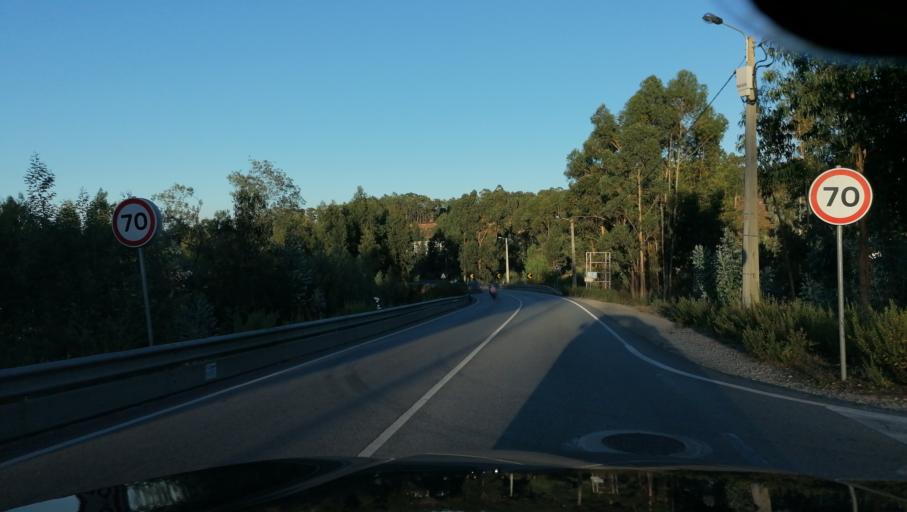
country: PT
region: Aveiro
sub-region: Oliveira do Bairro
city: Oia
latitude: 40.5437
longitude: -8.5278
